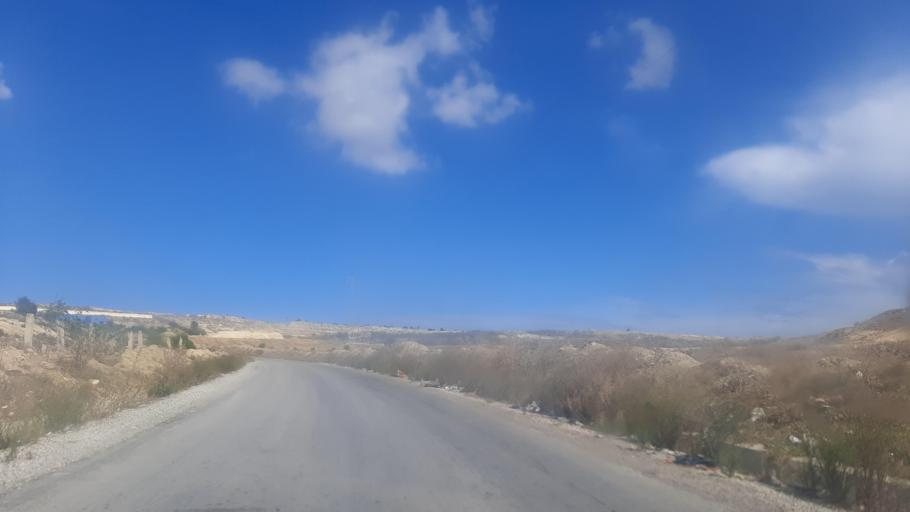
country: TN
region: Nabul
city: Nabeul
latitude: 36.4906
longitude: 10.7047
